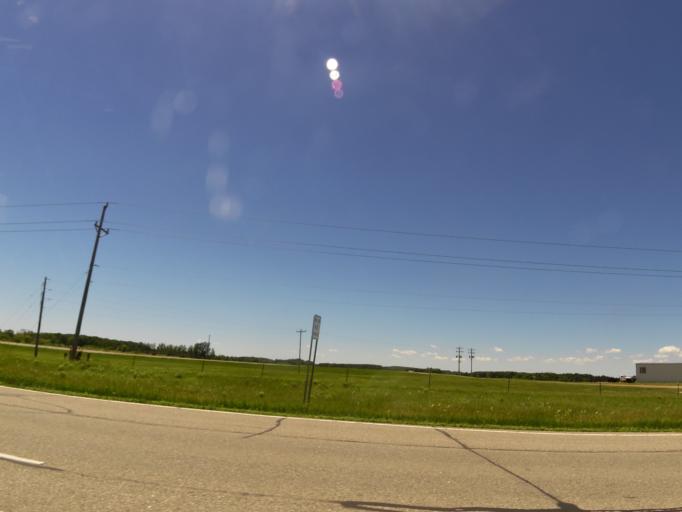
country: US
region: Minnesota
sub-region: Otter Tail County
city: Perham
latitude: 46.6297
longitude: -95.6280
